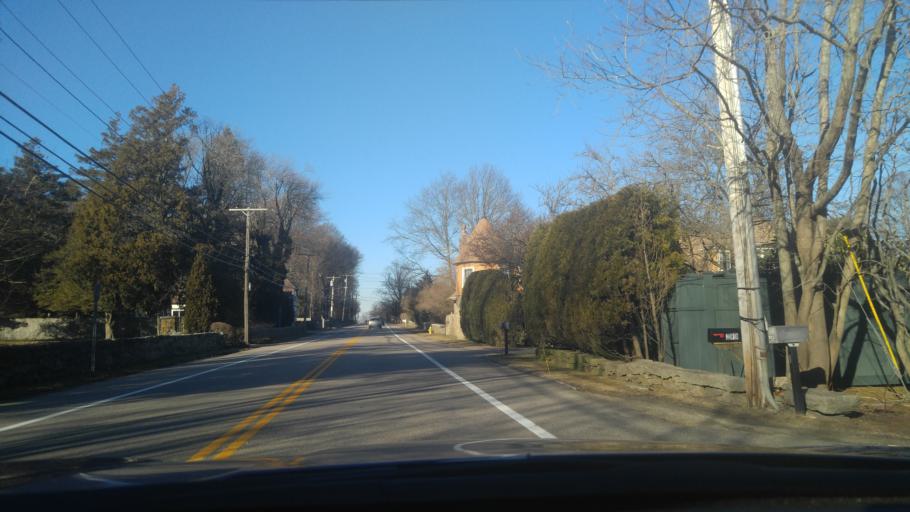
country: US
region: Rhode Island
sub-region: Washington County
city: Narragansett Pier
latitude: 41.4123
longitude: -71.4561
